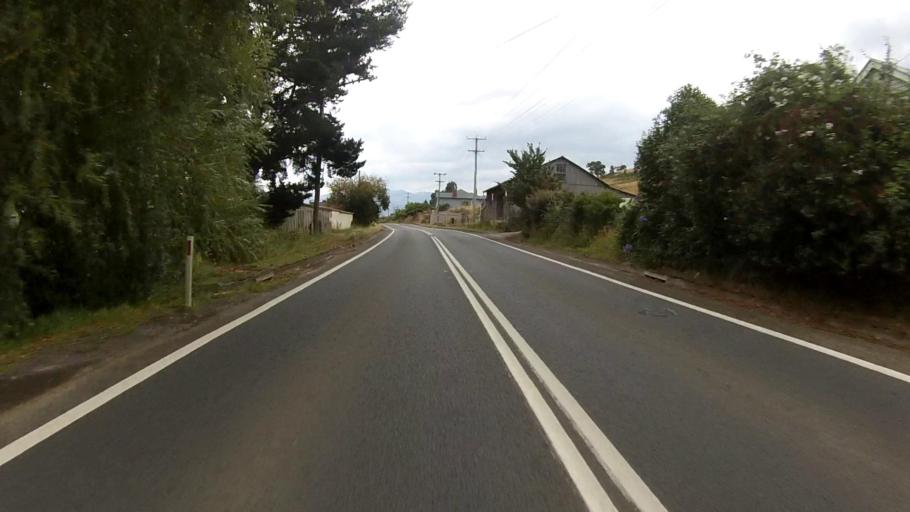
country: AU
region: Tasmania
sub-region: Huon Valley
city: Huonville
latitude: -43.0493
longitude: 147.0505
